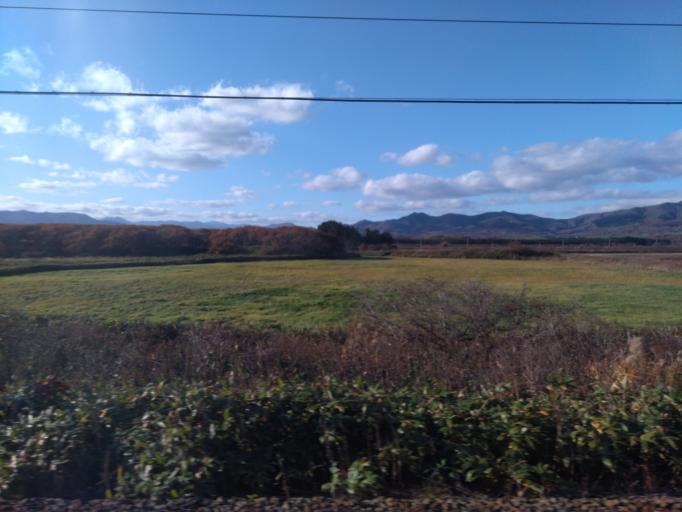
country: JP
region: Hokkaido
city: Niseko Town
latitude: 42.5392
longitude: 140.4048
